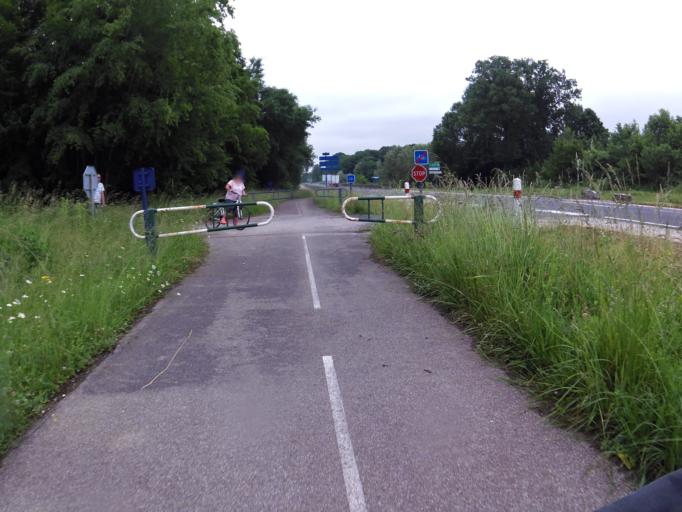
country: FR
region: Champagne-Ardenne
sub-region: Departement de la Haute-Marne
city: Laneuville-a-Remy
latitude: 48.5675
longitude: 4.8461
